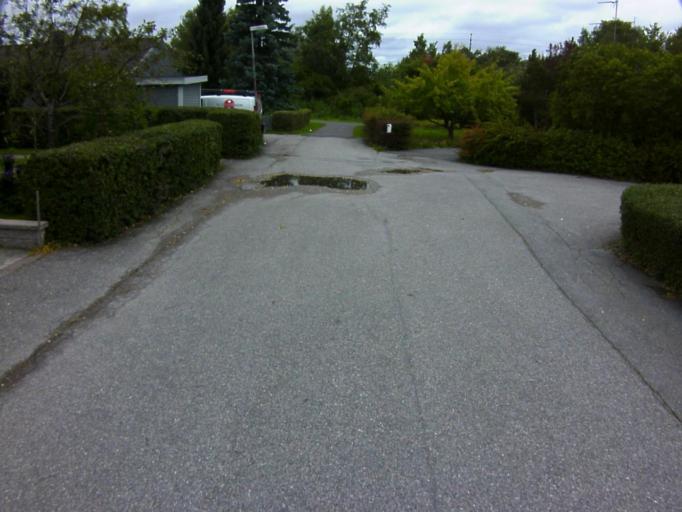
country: SE
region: Soedermanland
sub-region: Eskilstuna Kommun
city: Torshalla
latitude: 59.3809
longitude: 16.4719
